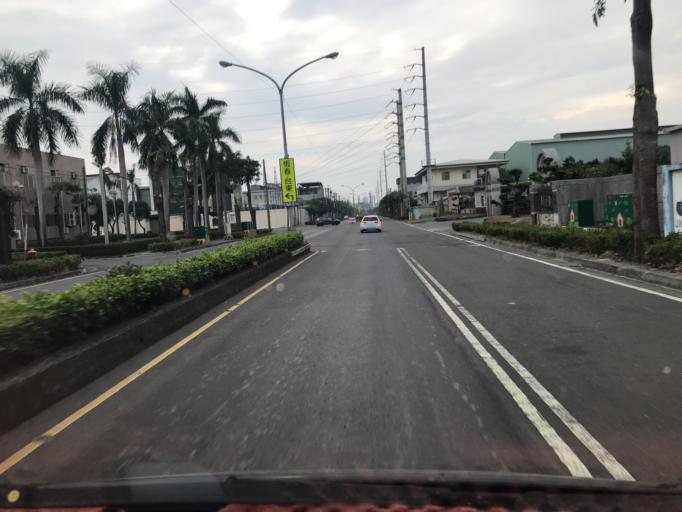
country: TW
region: Taiwan
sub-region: Pingtung
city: Pingtung
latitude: 22.4124
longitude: 120.5778
